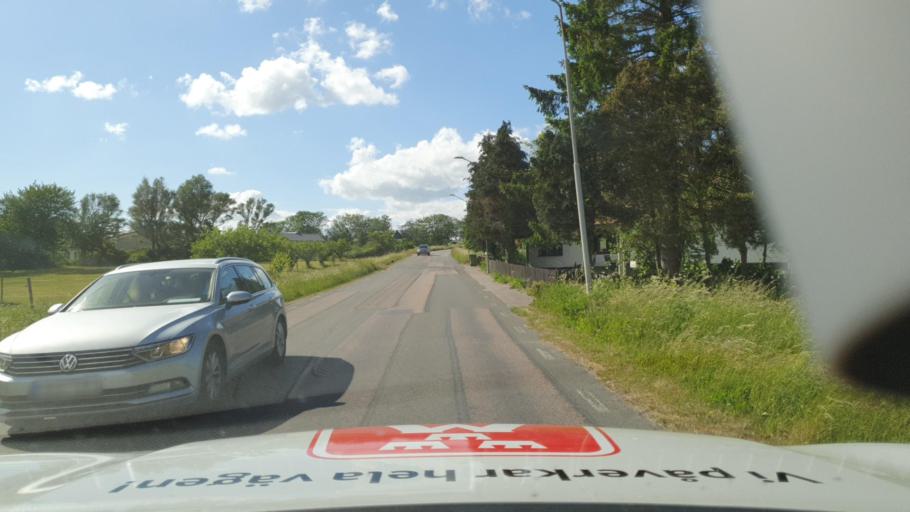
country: SE
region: Skane
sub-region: Simrishamns Kommun
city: Simrishamn
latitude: 55.5601
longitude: 14.3106
